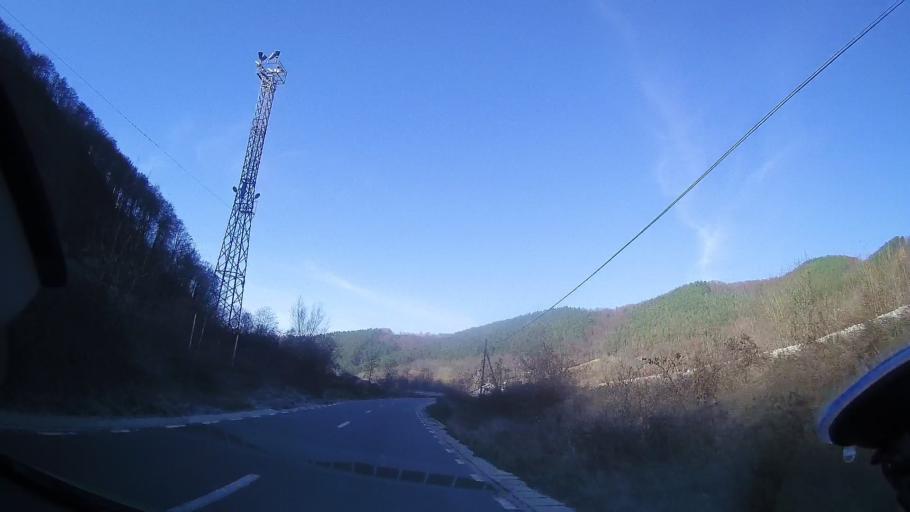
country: RO
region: Bihor
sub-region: Comuna Bratca
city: Bratca
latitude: 46.9255
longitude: 22.6498
